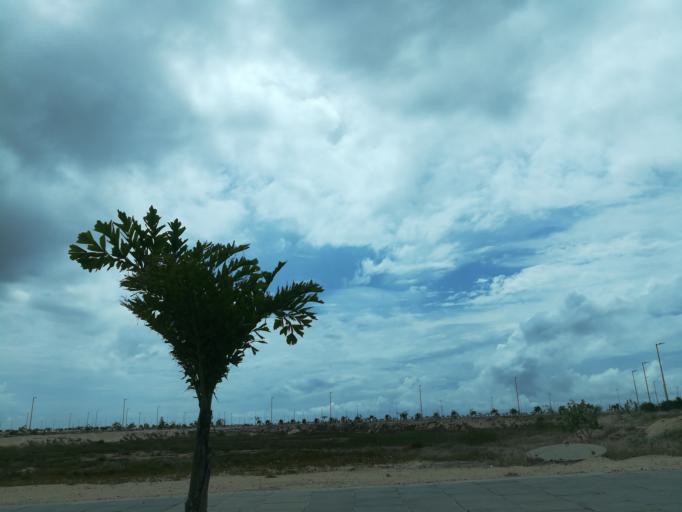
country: NG
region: Lagos
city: Lagos
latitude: 6.4100
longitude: 3.4113
